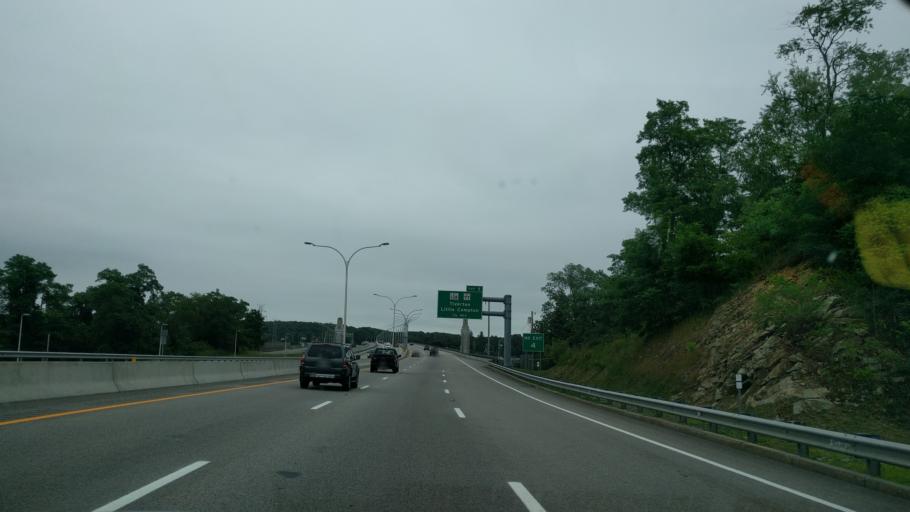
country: US
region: Rhode Island
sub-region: Newport County
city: Tiverton
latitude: 41.6381
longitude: -71.2201
